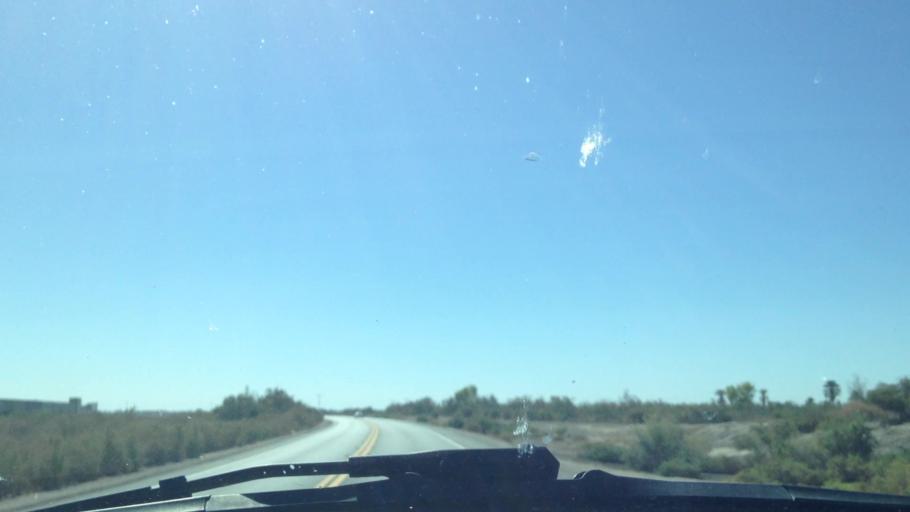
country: US
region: California
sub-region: Riverside County
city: Mecca
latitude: 33.5583
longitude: -116.0683
